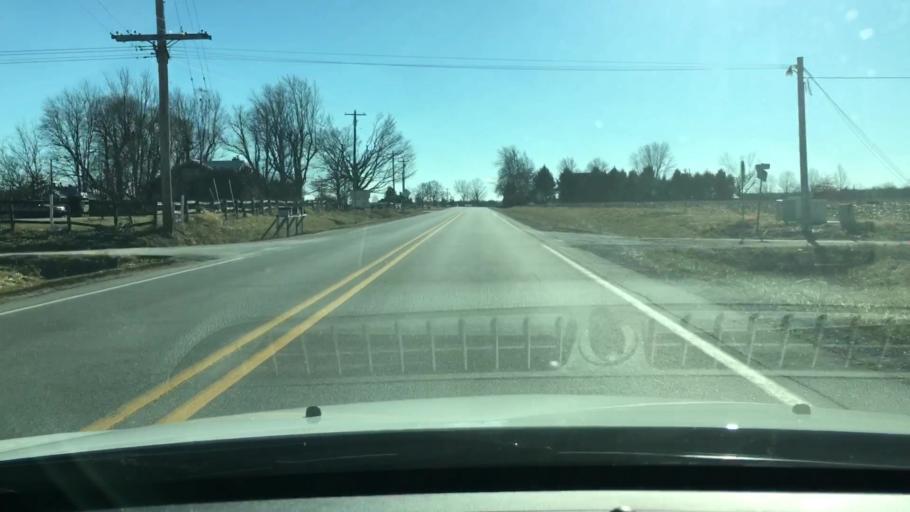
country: US
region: Illinois
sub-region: Pike County
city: Pittsfield
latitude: 39.6496
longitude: -90.7842
